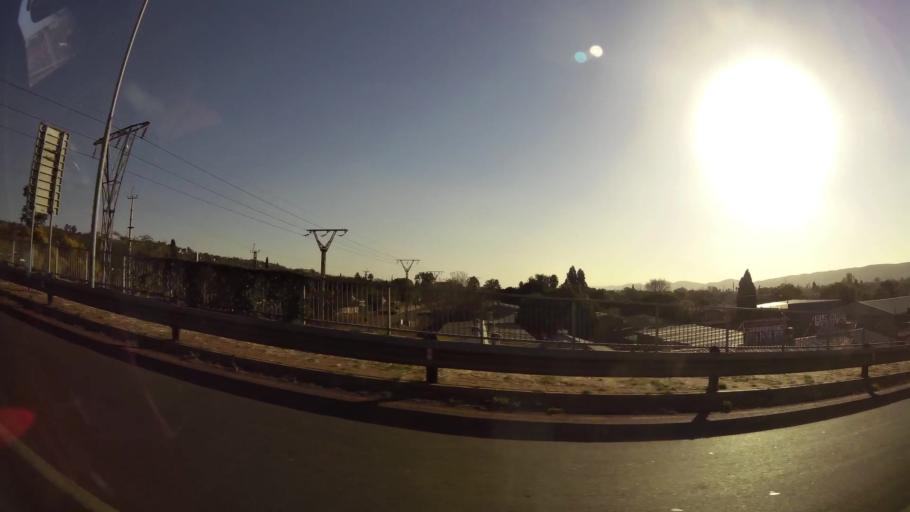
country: ZA
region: Gauteng
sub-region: City of Tshwane Metropolitan Municipality
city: Pretoria
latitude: -25.7195
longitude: 28.2423
